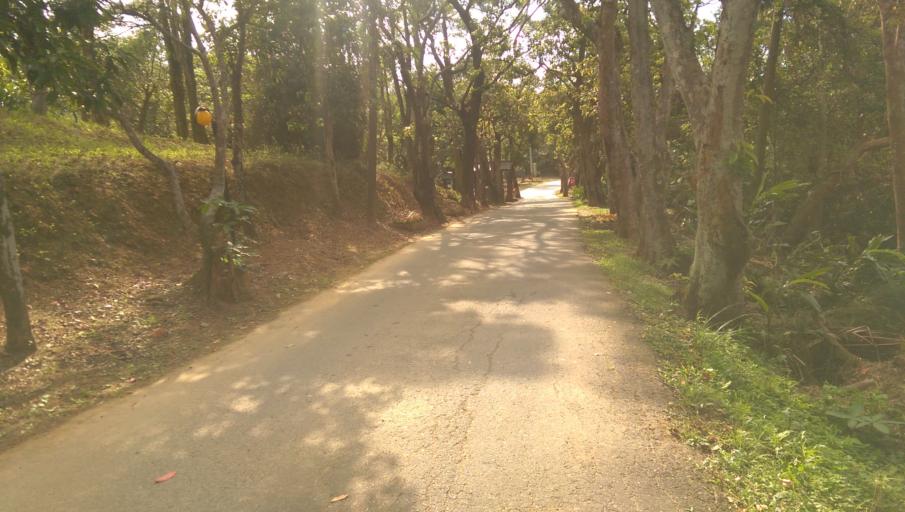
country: TW
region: Taipei
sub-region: Taipei
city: Banqiao
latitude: 24.9316
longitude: 121.5420
